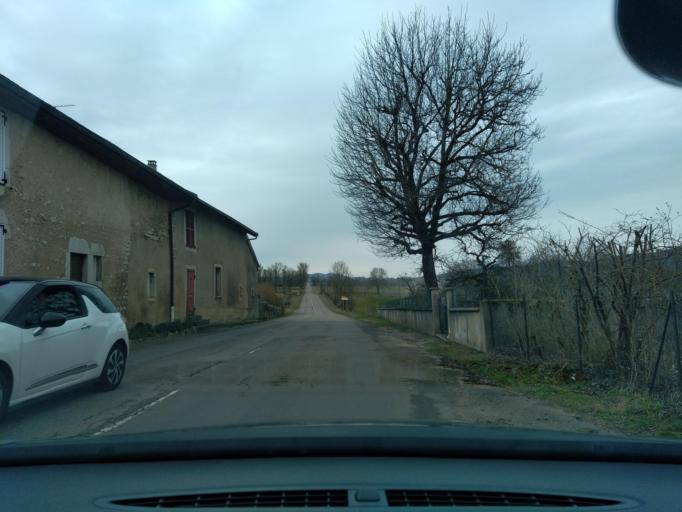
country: FR
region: Franche-Comte
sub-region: Departement du Jura
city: Arinthod
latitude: 46.3789
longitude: 5.5634
